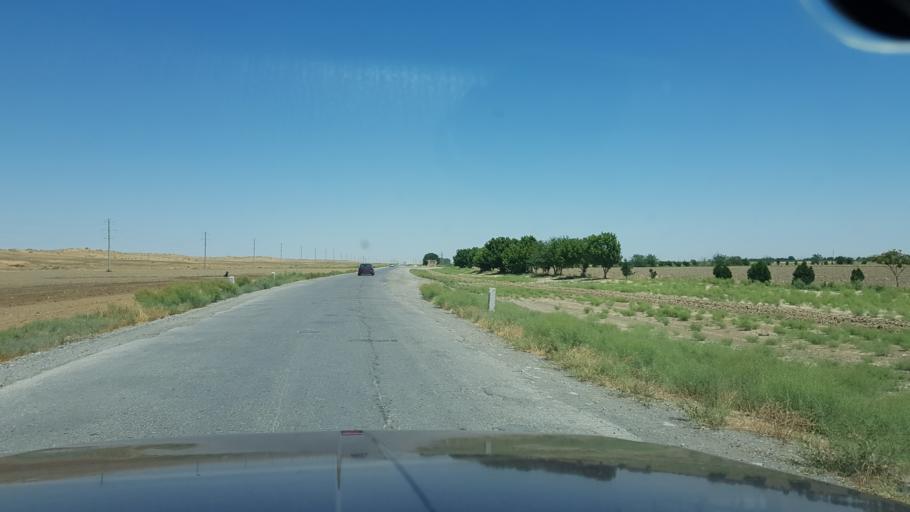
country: TM
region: Ahal
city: Annau
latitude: 37.8590
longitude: 58.7082
